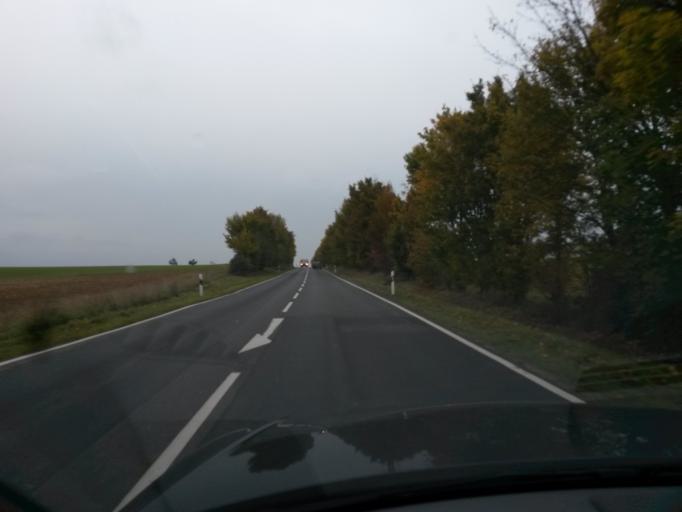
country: DE
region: Bavaria
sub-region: Regierungsbezirk Unterfranken
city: Estenfeld
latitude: 49.8397
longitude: 9.9849
